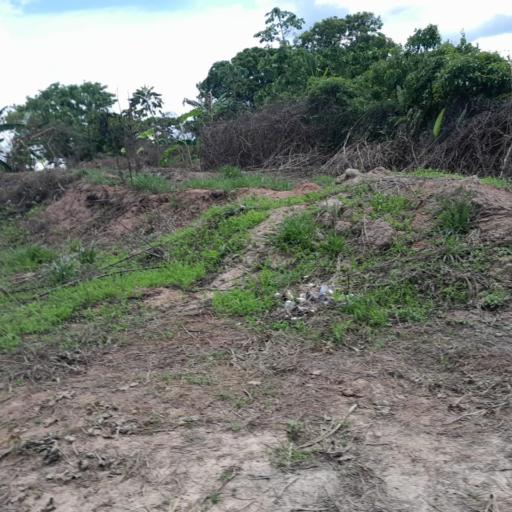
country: PE
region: Ucayali
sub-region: Provincia de Coronel Portillo
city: Puerto Callao
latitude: -8.2713
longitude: -74.6510
